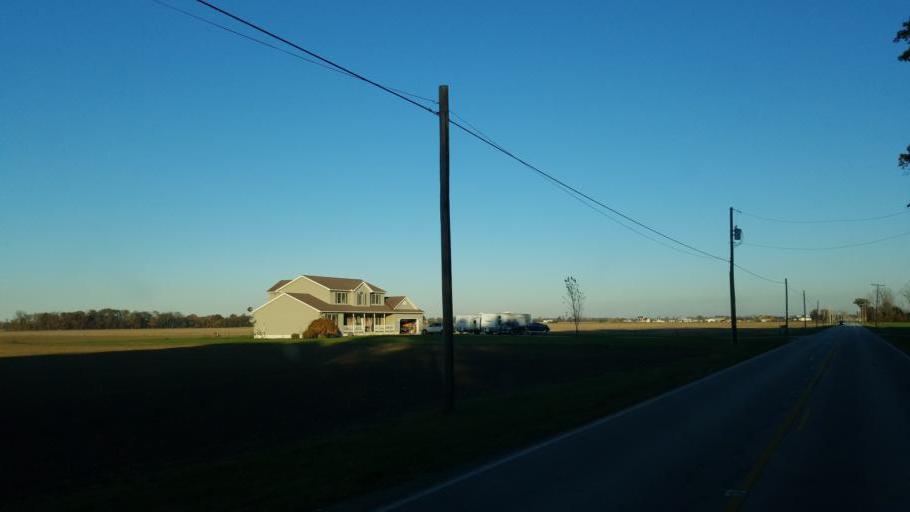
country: US
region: Ohio
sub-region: Sandusky County
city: Green Springs
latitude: 41.3068
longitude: -83.0435
